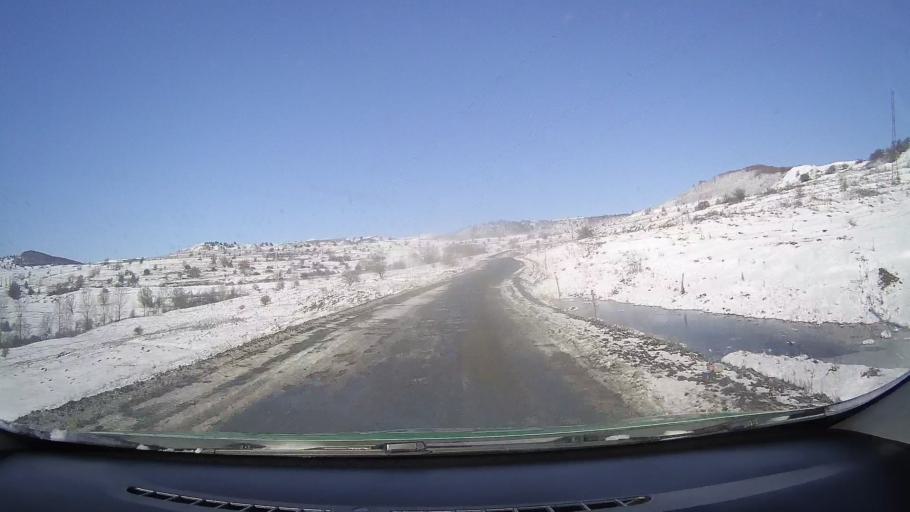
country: RO
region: Sibiu
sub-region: Comuna Avrig
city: Avrig
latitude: 45.7678
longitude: 24.3866
